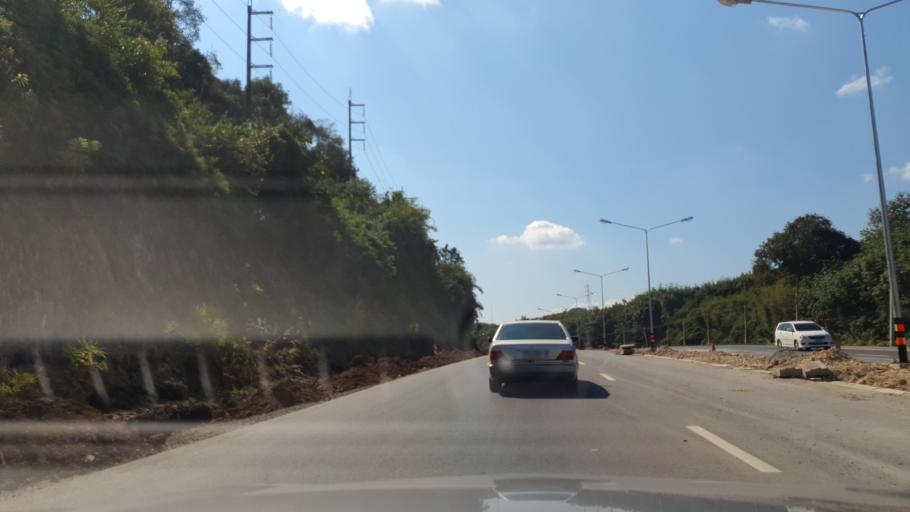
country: TH
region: Nan
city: Nan
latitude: 18.9178
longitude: 100.7653
